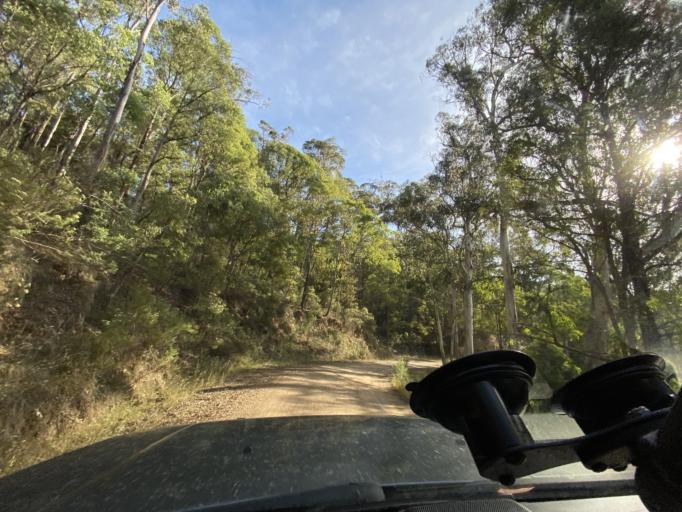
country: AU
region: Victoria
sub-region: Mansfield
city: Mansfield
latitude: -37.5172
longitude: 146.0944
